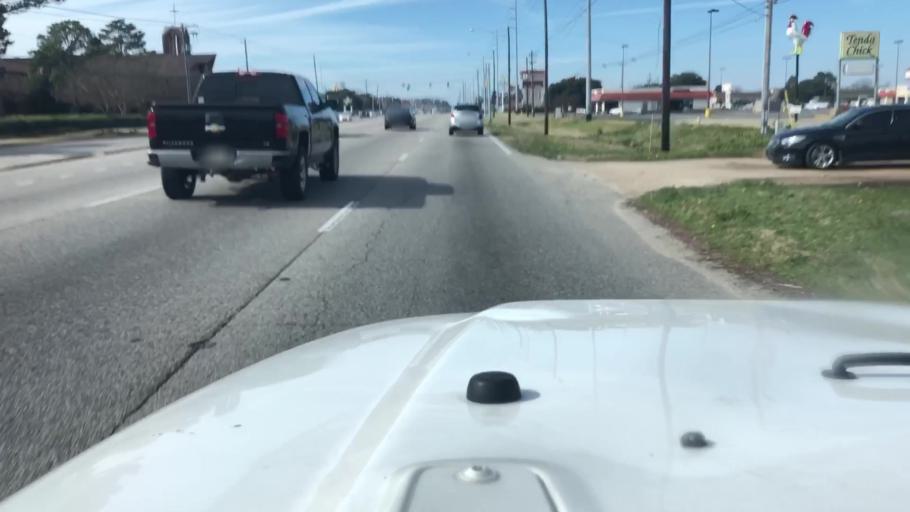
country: US
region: Alabama
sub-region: Montgomery County
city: Montgomery
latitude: 32.3824
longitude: -86.1956
